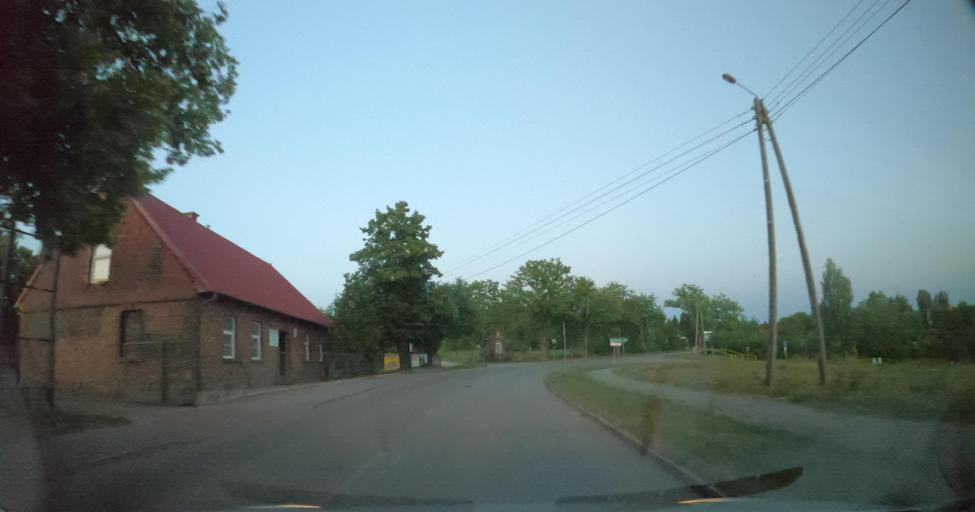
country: PL
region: Pomeranian Voivodeship
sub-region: Powiat wejherowski
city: Szemud
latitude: 54.4773
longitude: 18.2701
